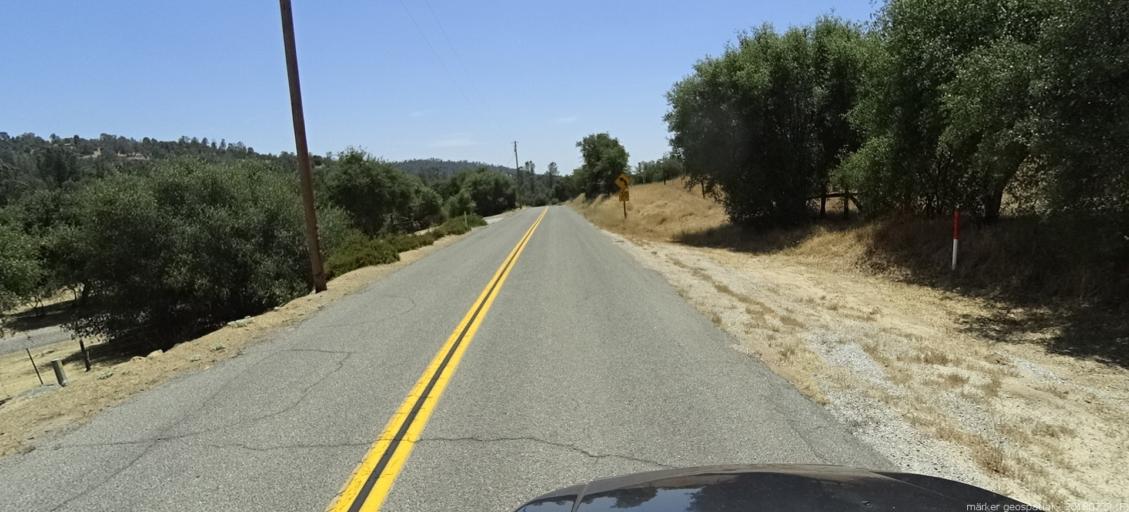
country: US
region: California
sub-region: Madera County
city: Yosemite Lakes
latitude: 37.2089
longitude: -119.7284
